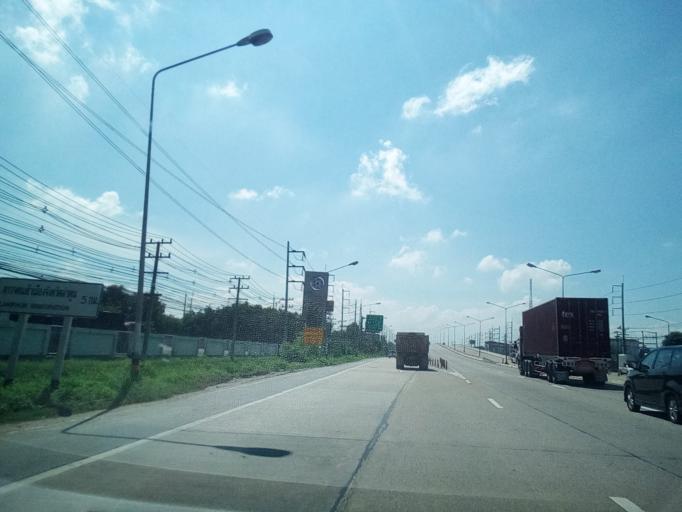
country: TH
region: Lamphun
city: Lamphun
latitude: 18.5931
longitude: 99.0427
